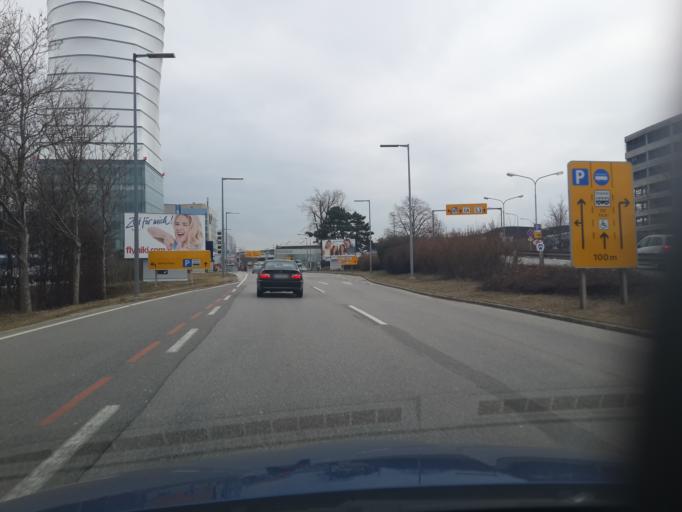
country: AT
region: Lower Austria
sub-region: Politischer Bezirk Wien-Umgebung
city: Fischamend Dorf
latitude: 48.1233
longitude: 16.5599
